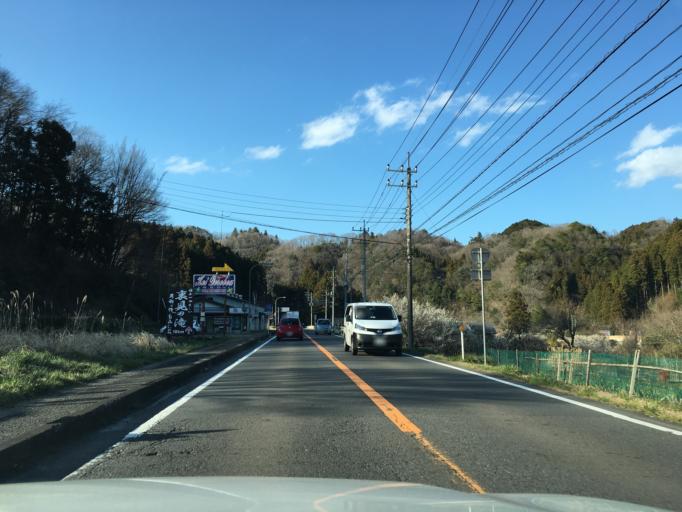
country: JP
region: Ibaraki
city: Daigo
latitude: 36.7331
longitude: 140.3901
